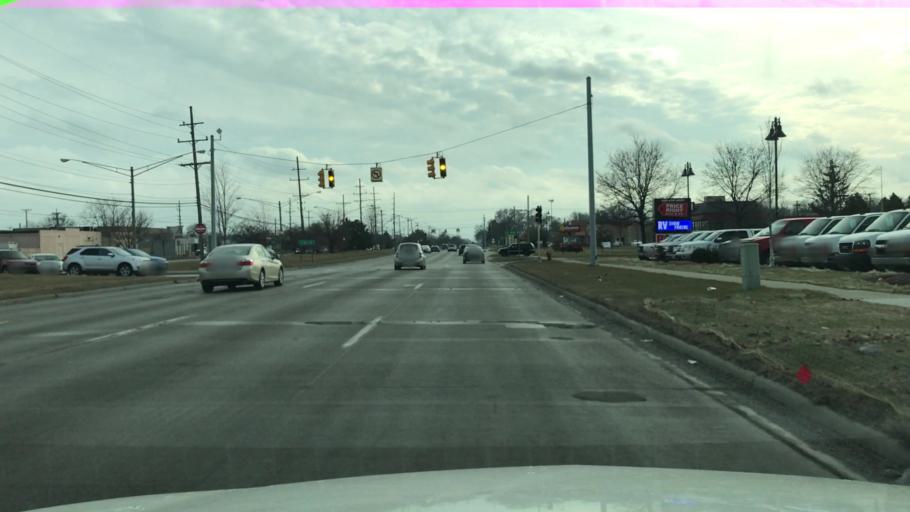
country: US
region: Michigan
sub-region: Macomb County
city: Sterling Heights
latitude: 42.5529
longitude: -83.0488
